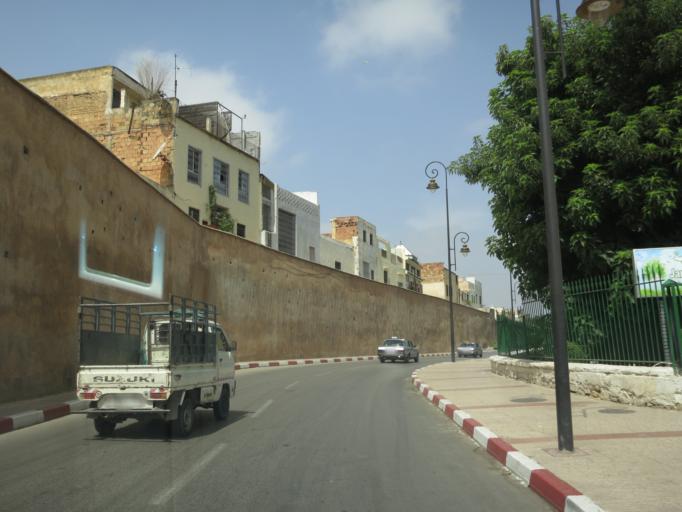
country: MA
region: Meknes-Tafilalet
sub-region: Meknes
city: Meknes
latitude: 33.8955
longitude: -5.5605
